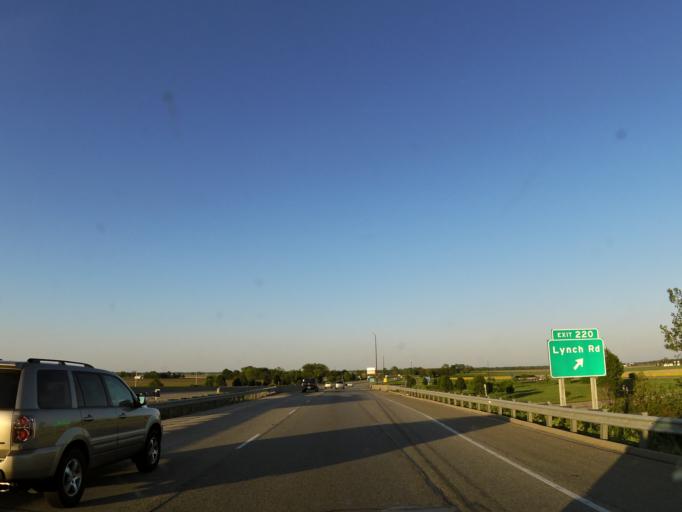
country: US
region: Illinois
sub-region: Vermilion County
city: Danville
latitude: 40.1169
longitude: -87.5391
